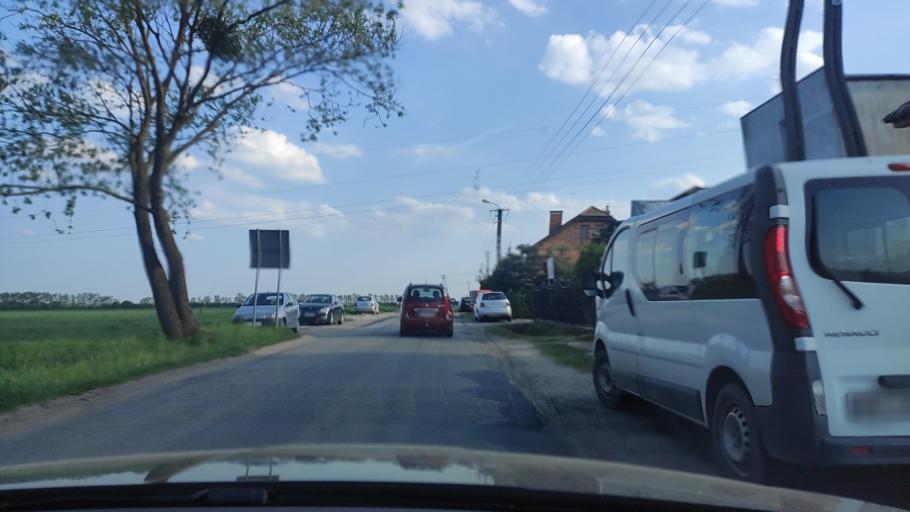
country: PL
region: Greater Poland Voivodeship
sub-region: Powiat poznanski
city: Kleszczewo
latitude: 52.3778
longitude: 17.1664
